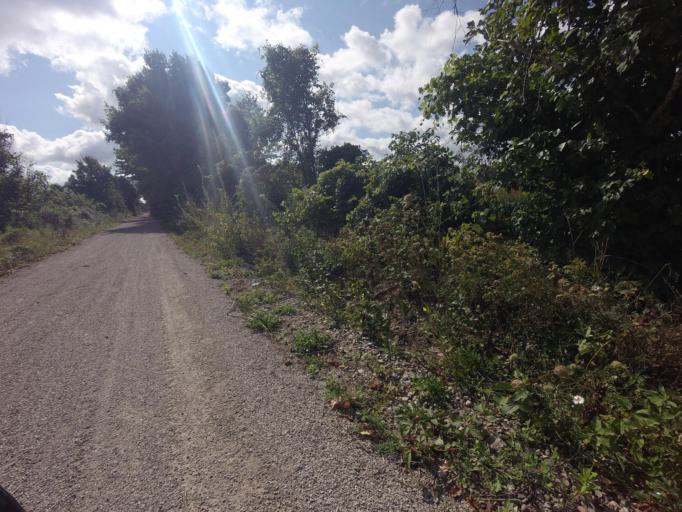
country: CA
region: Ontario
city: Huron East
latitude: 43.7230
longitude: -81.4035
